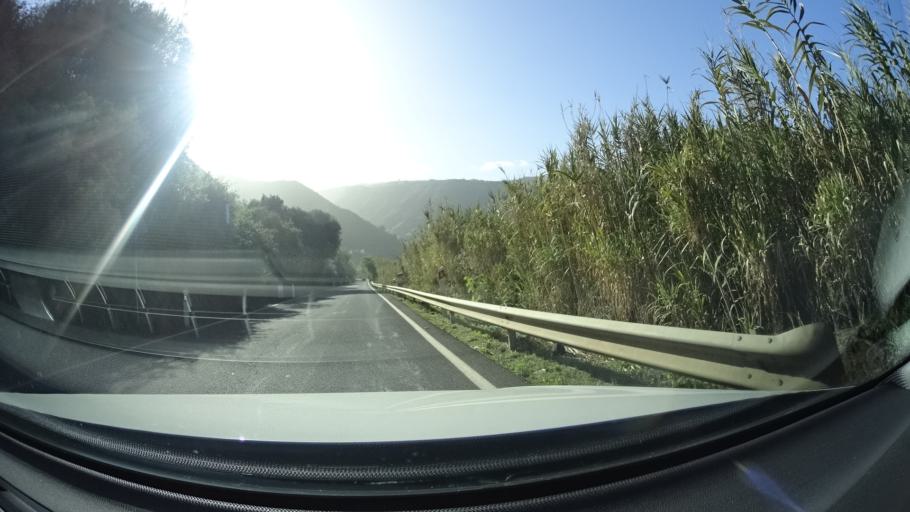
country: ES
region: Canary Islands
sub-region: Provincia de Las Palmas
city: Vega de San Mateo
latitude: 28.0175
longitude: -15.5470
